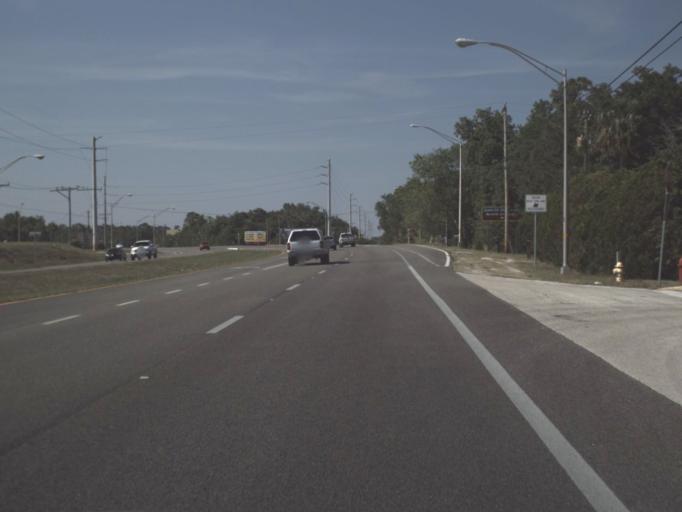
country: US
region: Florida
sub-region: Brevard County
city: Port Saint John
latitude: 28.5084
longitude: -80.7841
